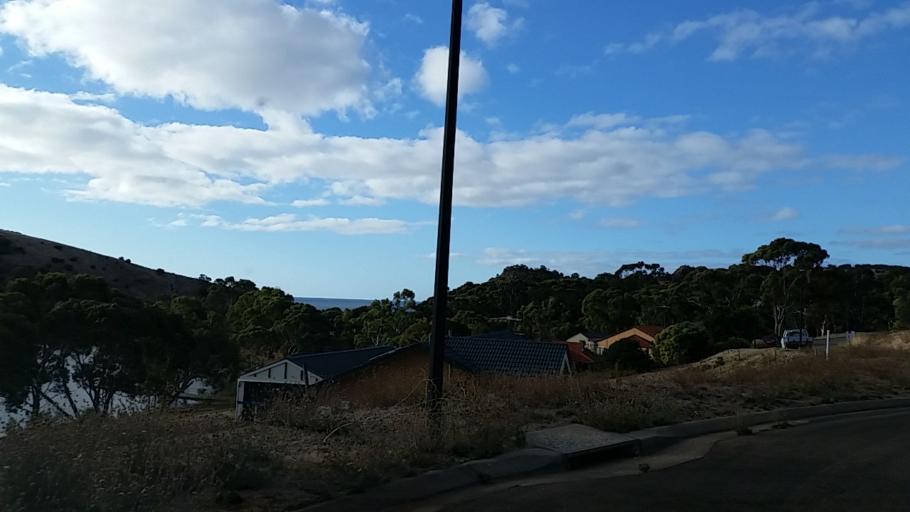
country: AU
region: South Australia
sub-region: Yankalilla
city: Normanville
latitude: -35.5079
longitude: 138.2445
